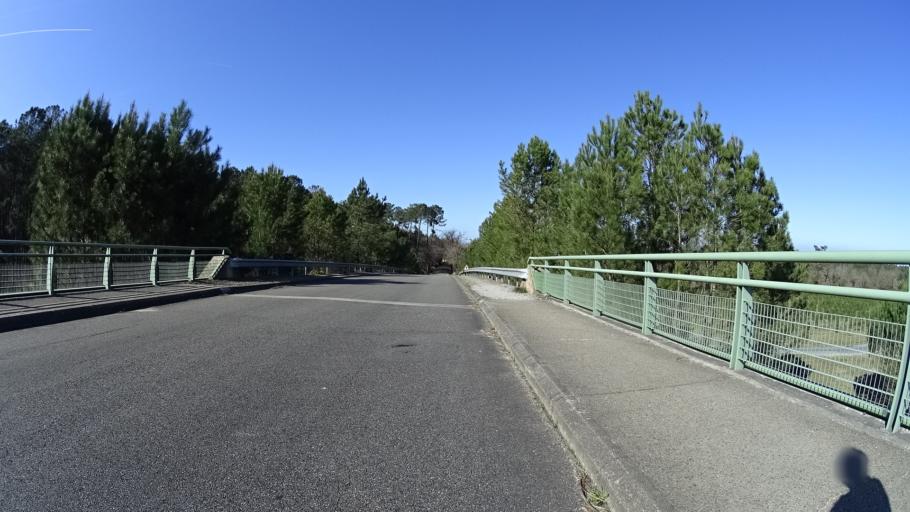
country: FR
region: Aquitaine
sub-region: Departement des Landes
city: Mees
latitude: 43.7384
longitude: -1.0961
